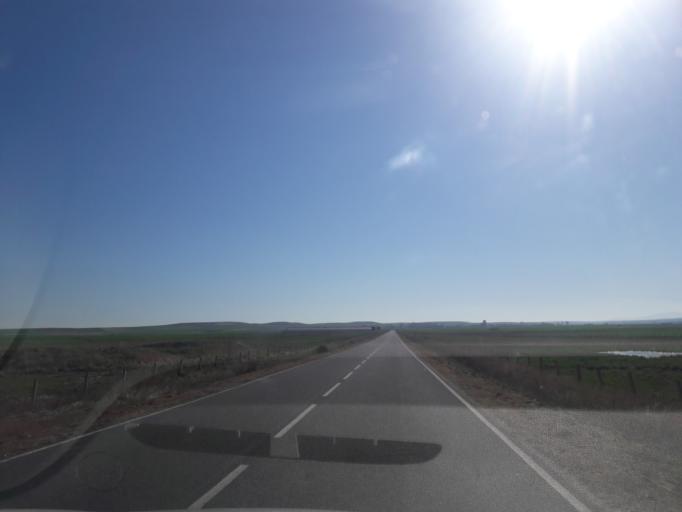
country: ES
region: Castille and Leon
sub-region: Provincia de Salamanca
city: Santiago de la Puebla
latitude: 40.8105
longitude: -5.2501
